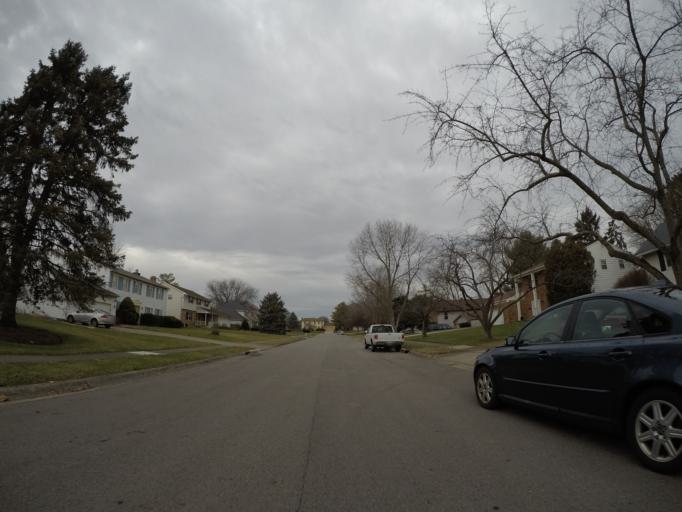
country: US
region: Ohio
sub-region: Franklin County
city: Upper Arlington
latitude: 40.0513
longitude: -83.0725
